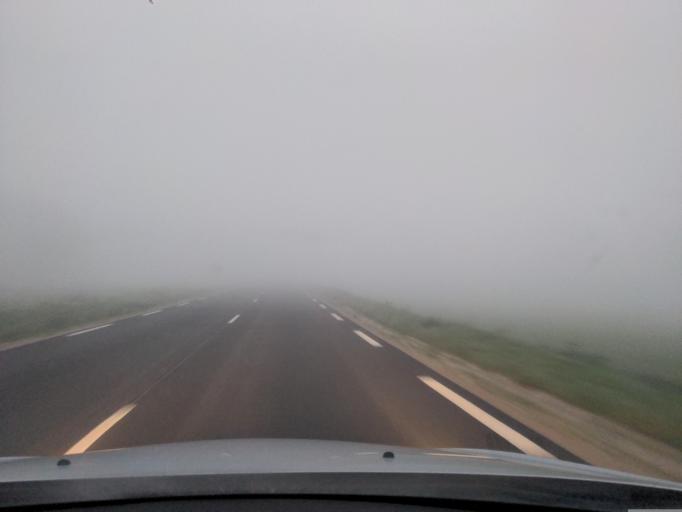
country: FR
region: Champagne-Ardenne
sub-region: Departement de la Haute-Marne
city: Langres
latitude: 47.8208
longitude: 5.3083
